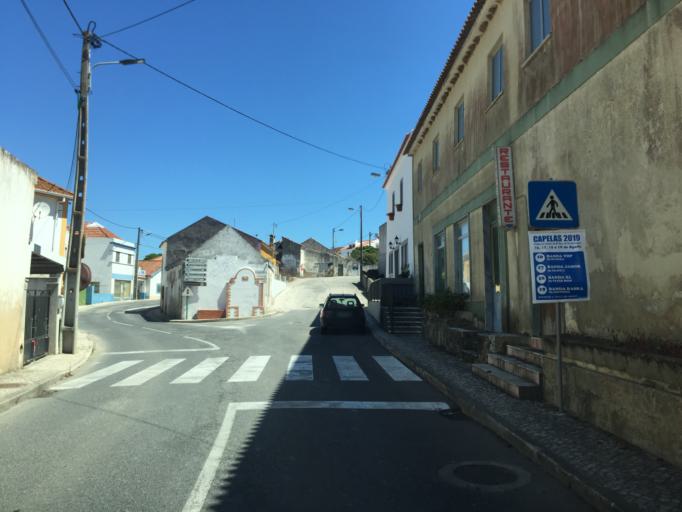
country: PT
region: Lisbon
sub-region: Torres Vedras
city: A dos Cunhados
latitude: 39.1783
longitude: -9.3191
